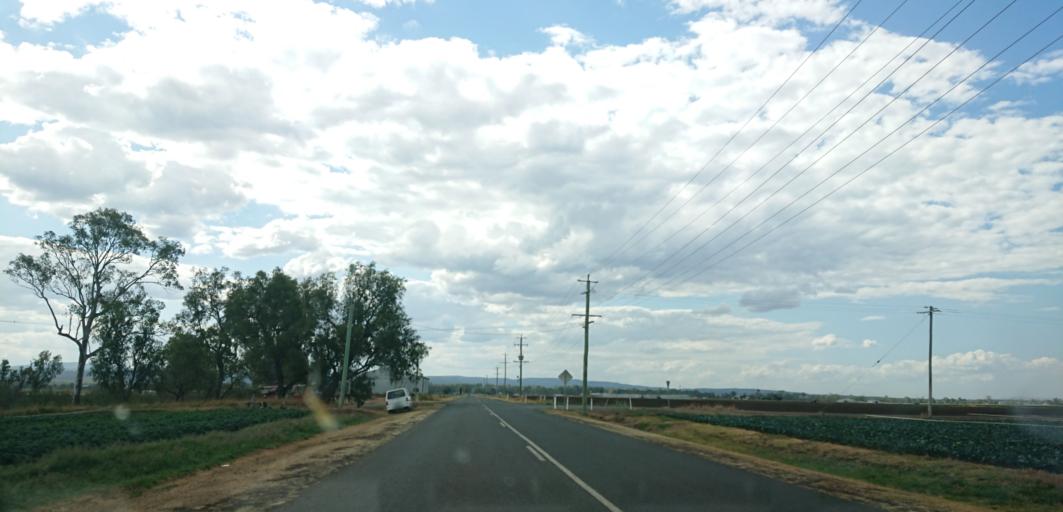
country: AU
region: Queensland
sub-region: Lockyer Valley
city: Gatton
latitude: -27.5909
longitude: 152.2270
